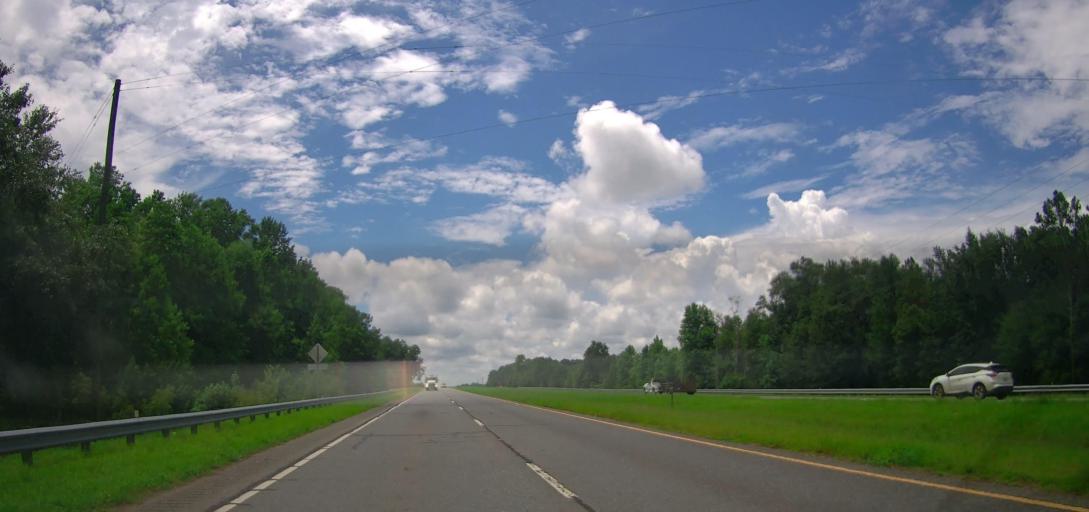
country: US
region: Georgia
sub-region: Dodge County
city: Eastman
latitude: 32.1760
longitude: -83.1702
